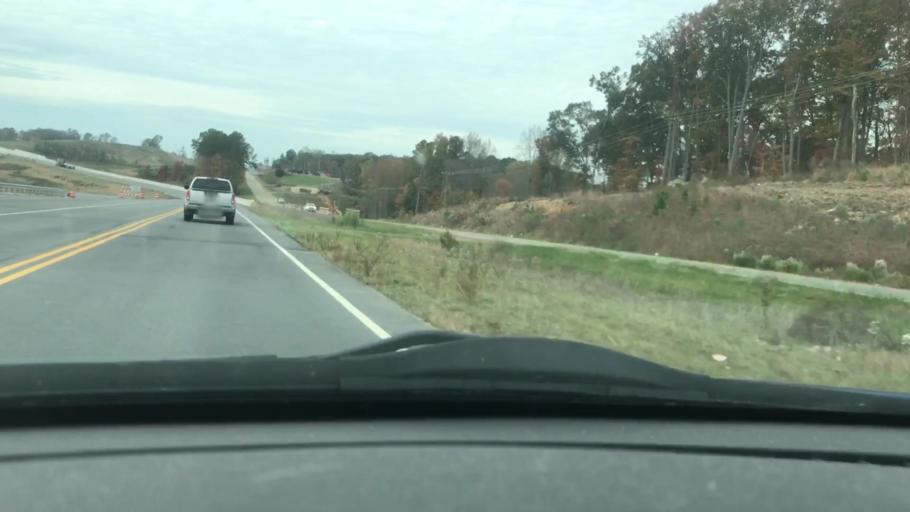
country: US
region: North Carolina
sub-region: Randolph County
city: Asheboro
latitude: 35.6962
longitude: -79.8615
